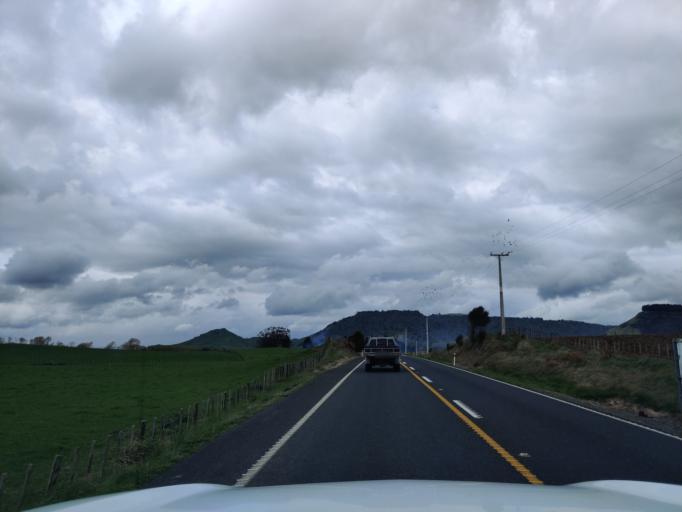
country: NZ
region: Manawatu-Wanganui
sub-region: Ruapehu District
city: Waiouru
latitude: -39.4892
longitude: 175.2959
